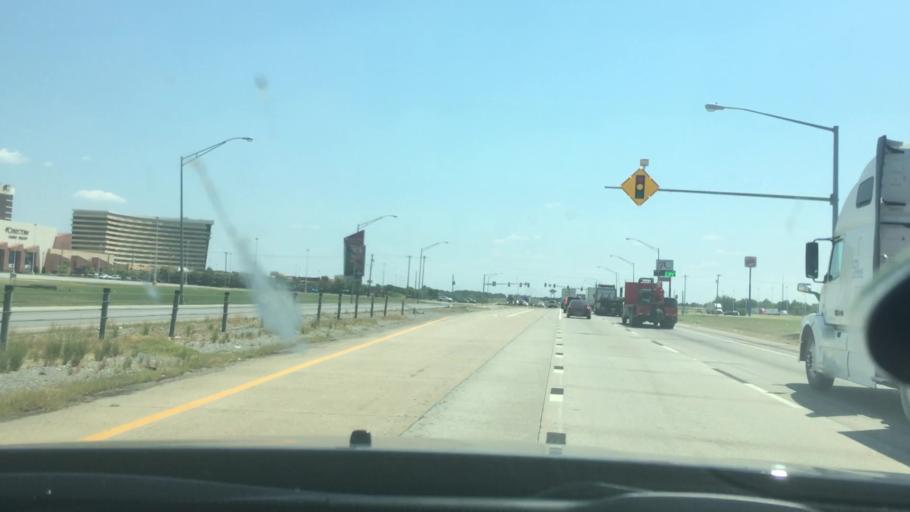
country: US
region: Oklahoma
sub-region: Bryan County
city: Calera
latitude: 33.9569
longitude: -96.4167
